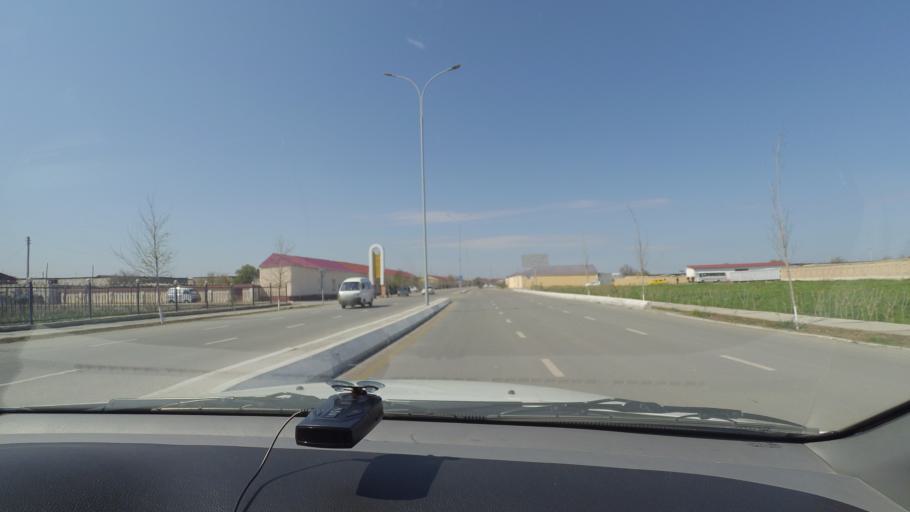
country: UZ
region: Bukhara
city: Kogon
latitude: 39.7999
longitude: 64.5344
